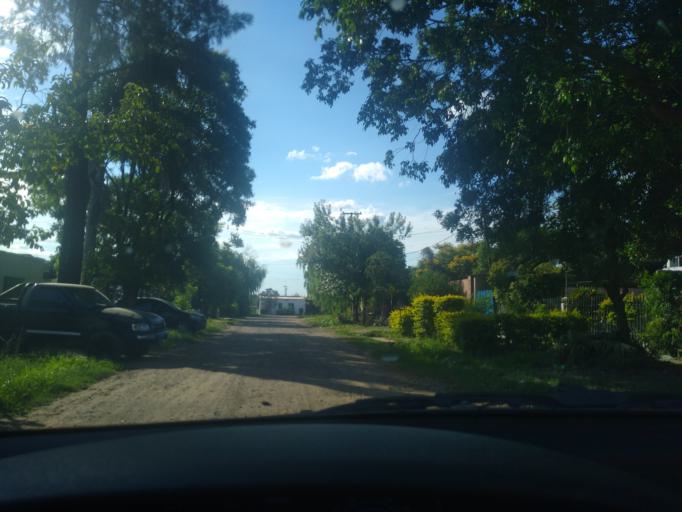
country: AR
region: Chaco
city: Barranqueras
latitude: -27.4717
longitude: -58.9346
